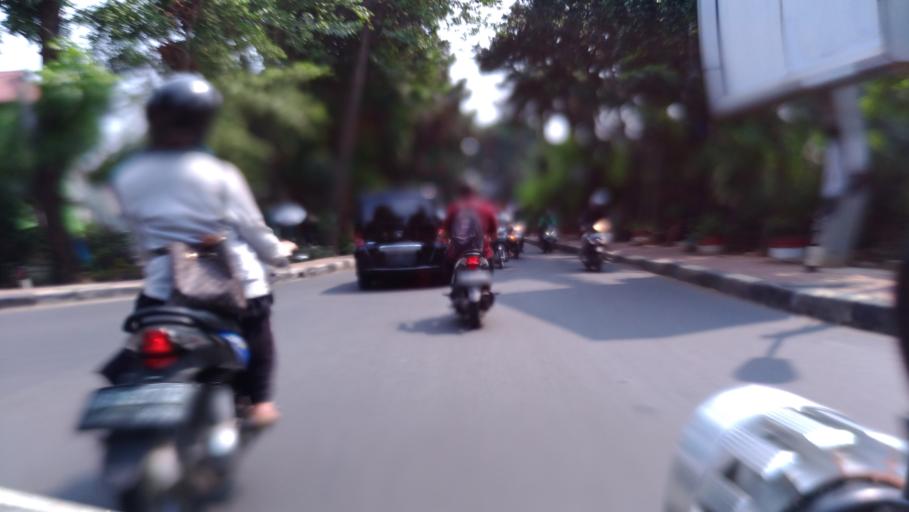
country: ID
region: West Java
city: Cileungsir
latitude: -6.3522
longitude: 106.8879
